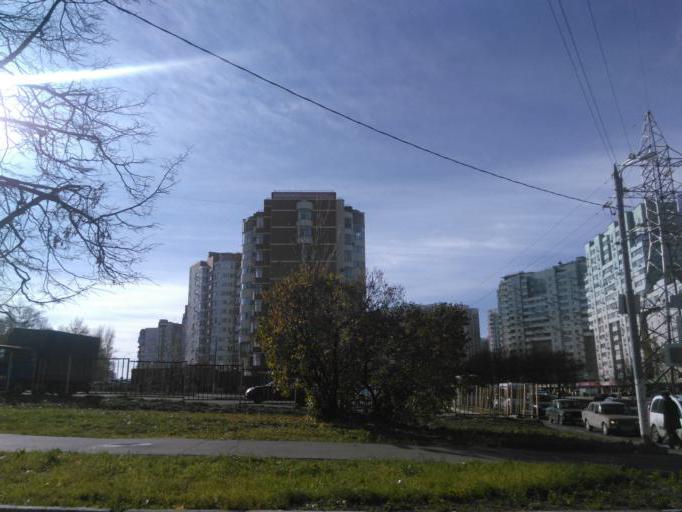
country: RU
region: Moskovskaya
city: Semenovskoye
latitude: 55.6735
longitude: 37.5450
